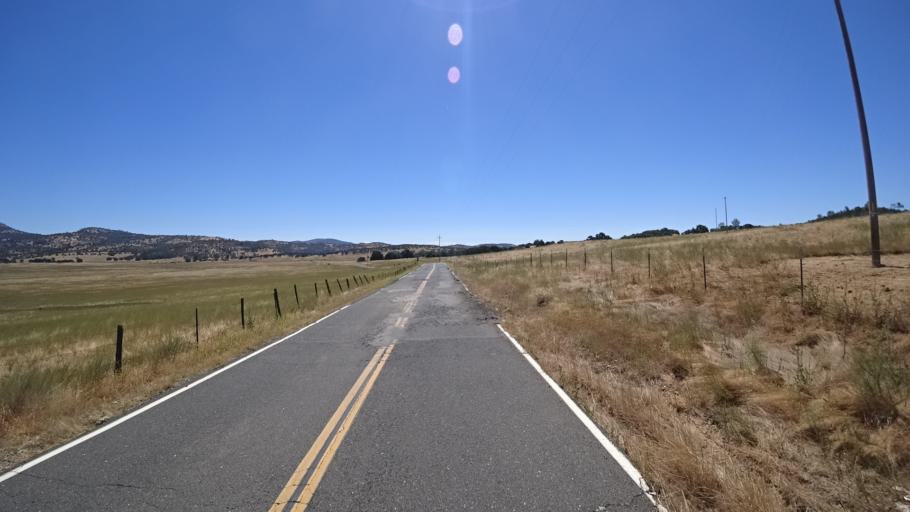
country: US
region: California
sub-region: Calaveras County
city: Copperopolis
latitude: 38.0208
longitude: -120.7111
